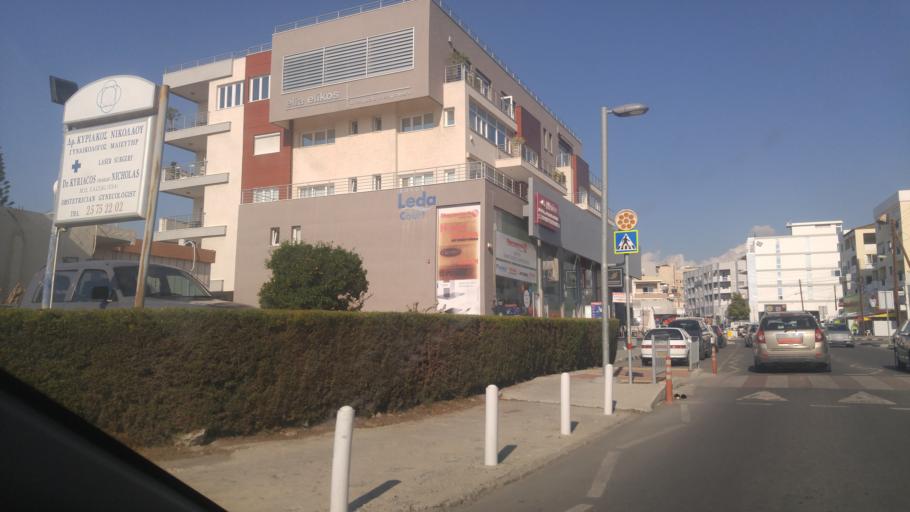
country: CY
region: Limassol
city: Limassol
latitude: 34.6957
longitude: 33.0505
